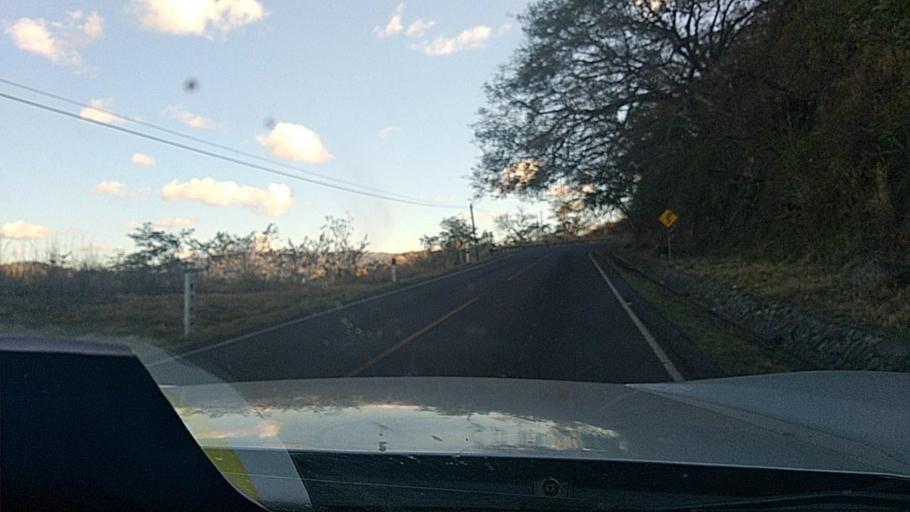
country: NI
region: Esteli
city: Condega
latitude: 13.2554
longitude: -86.3521
